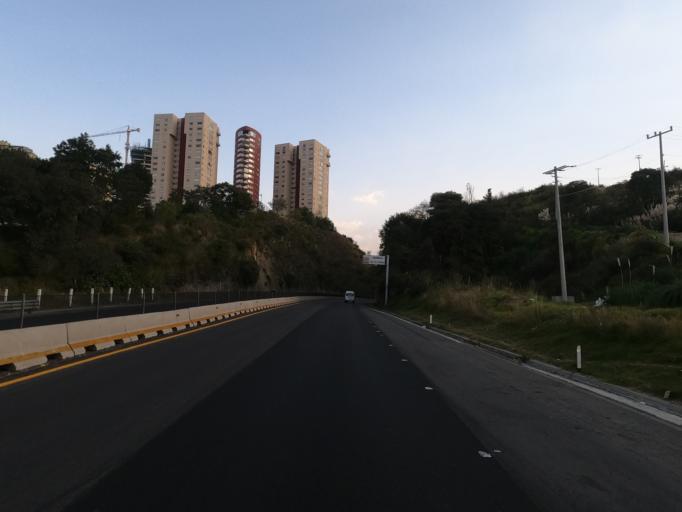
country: MX
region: Mexico
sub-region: Naucalpan de Juarez
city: Ejido el Castillo
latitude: 19.4289
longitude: -99.2957
